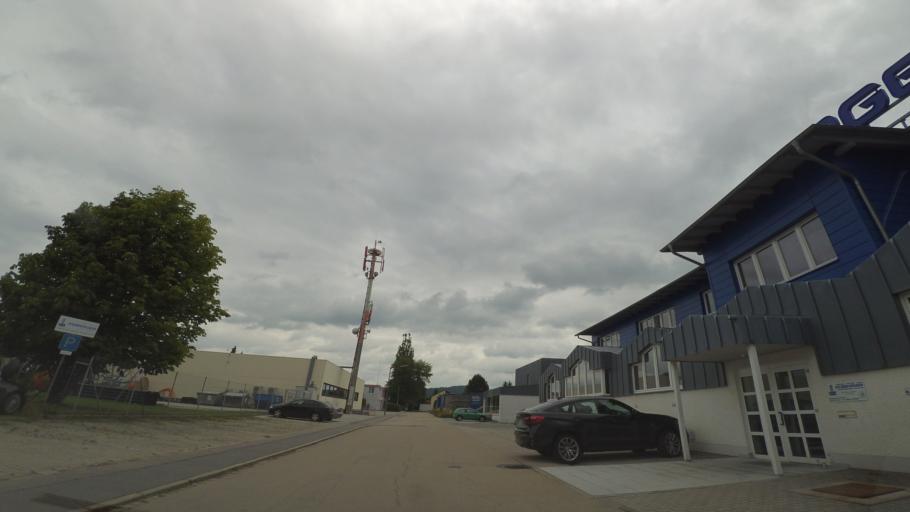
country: DE
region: Bavaria
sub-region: Upper Palatinate
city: Cham
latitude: 49.2037
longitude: 12.6665
